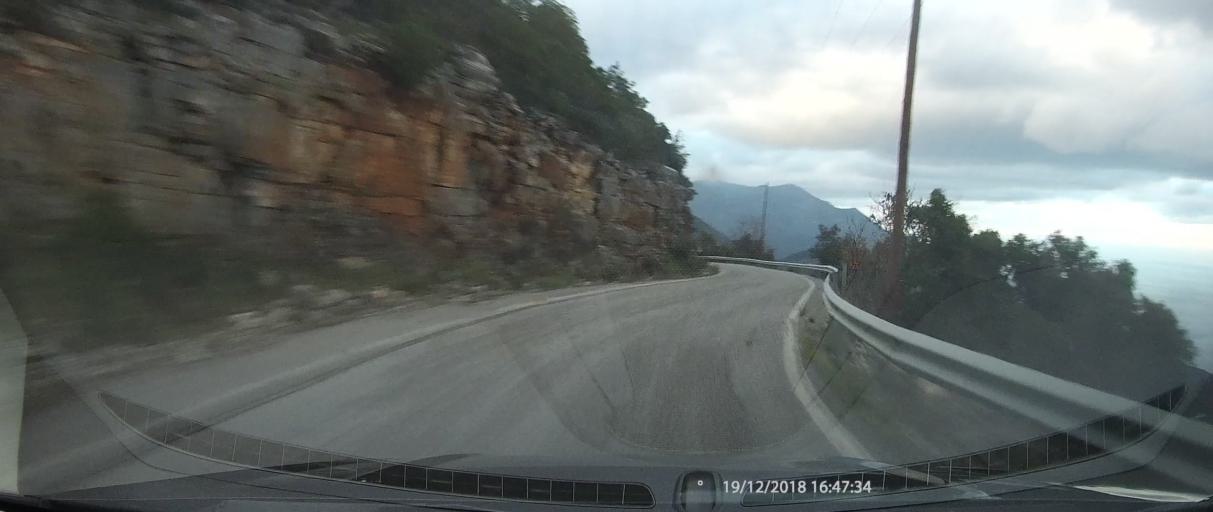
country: GR
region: Peloponnese
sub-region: Nomos Lakonias
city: Sykea
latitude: 36.9292
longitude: 23.0043
